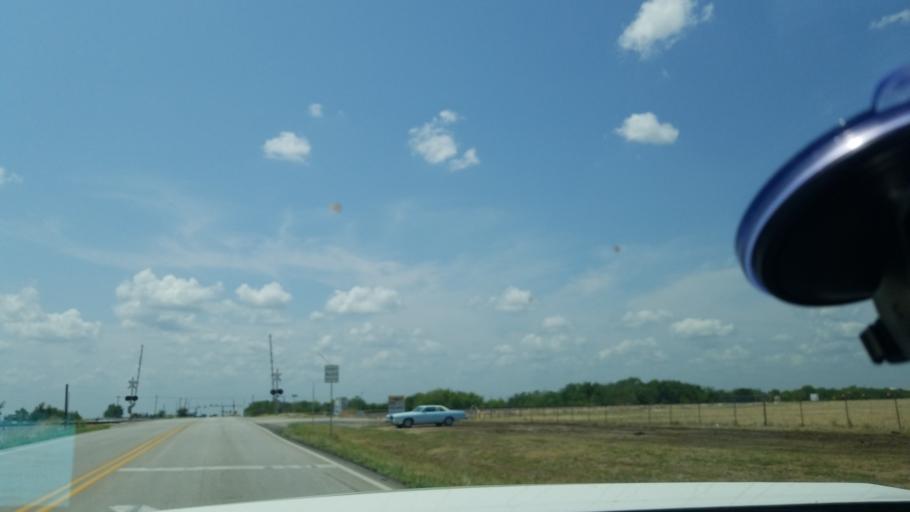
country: US
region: Texas
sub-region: Tarrant County
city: Eagle Mountain
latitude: 32.9245
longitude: -97.4073
